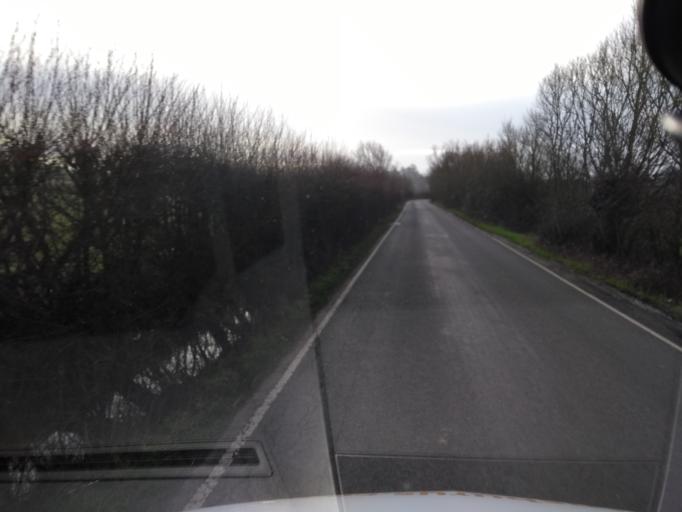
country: GB
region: England
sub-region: Somerset
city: Creech Saint Michael
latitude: 51.0326
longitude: -2.9742
